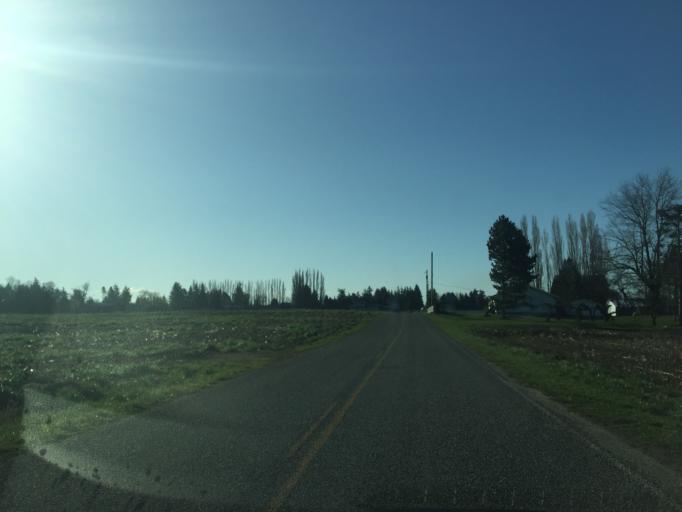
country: US
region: Washington
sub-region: Whatcom County
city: Lynden
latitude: 48.9151
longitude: -122.4642
